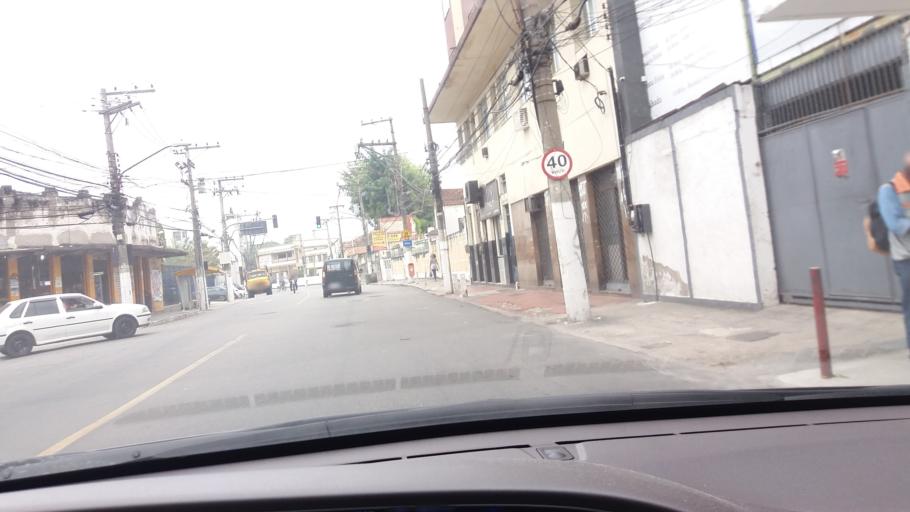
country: BR
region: Rio de Janeiro
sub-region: Niteroi
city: Niteroi
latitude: -22.8608
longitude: -43.1025
